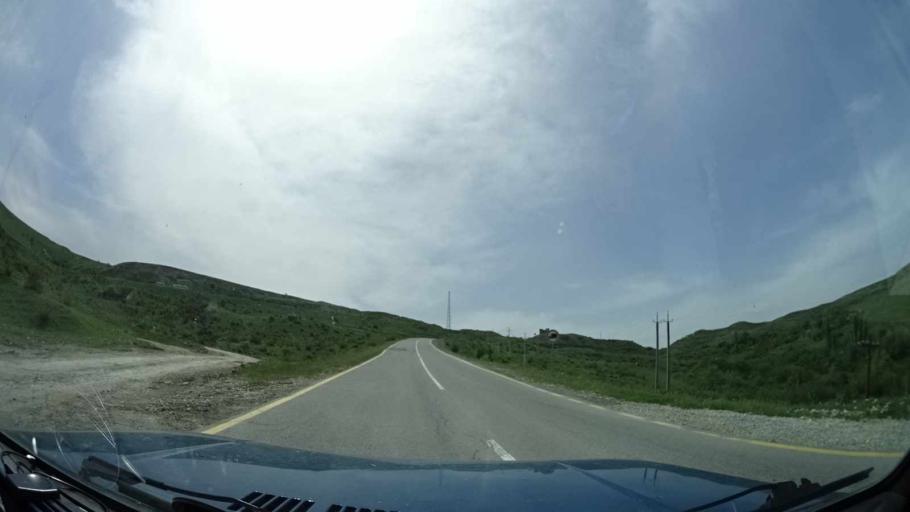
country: AZ
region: Xizi
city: Khyzy
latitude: 40.9047
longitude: 49.1173
